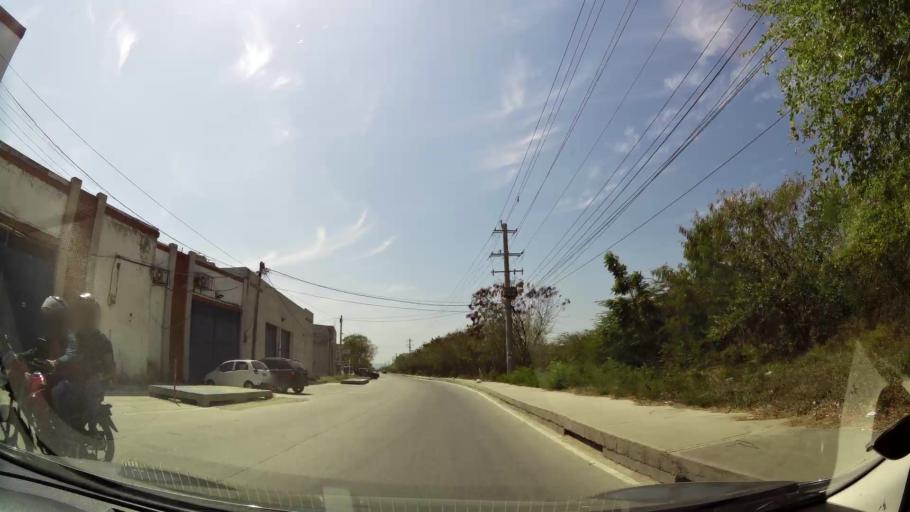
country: CO
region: Atlantico
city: Barranquilla
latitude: 10.9801
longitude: -74.8464
